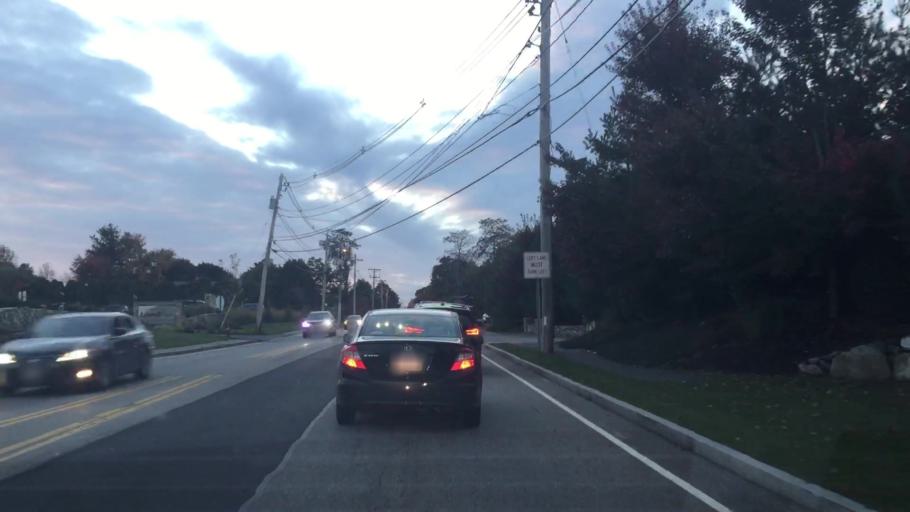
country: US
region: Massachusetts
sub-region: Middlesex County
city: Tewksbury
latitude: 42.6428
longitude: -71.2401
